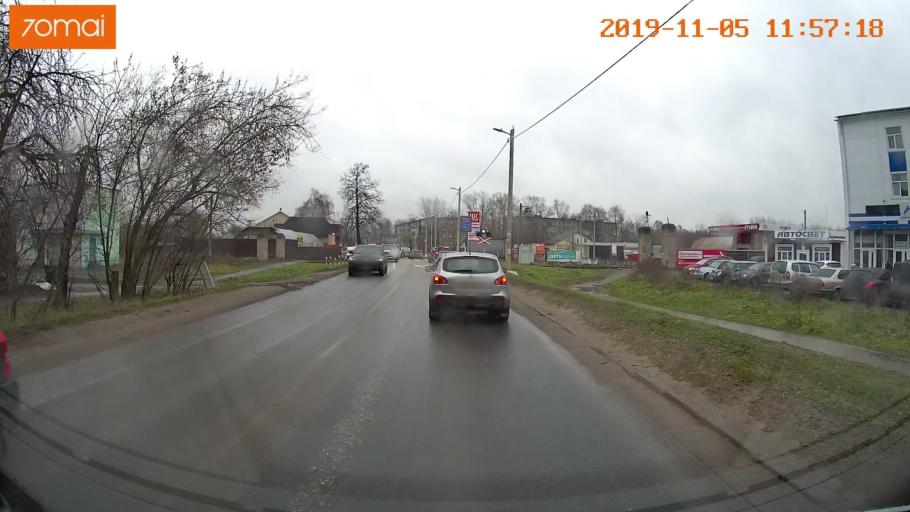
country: RU
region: Ivanovo
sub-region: Gorod Ivanovo
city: Ivanovo
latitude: 56.9835
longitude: 41.0341
